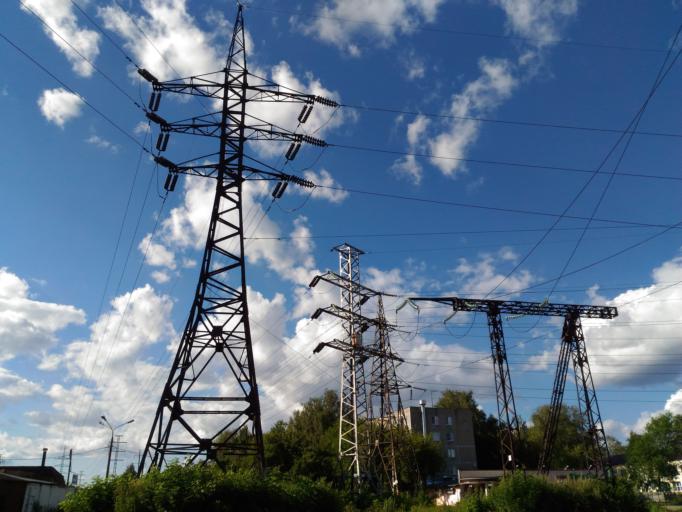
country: RU
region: Nizjnij Novgorod
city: Nizhniy Novgorod
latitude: 56.3196
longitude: 43.8804
